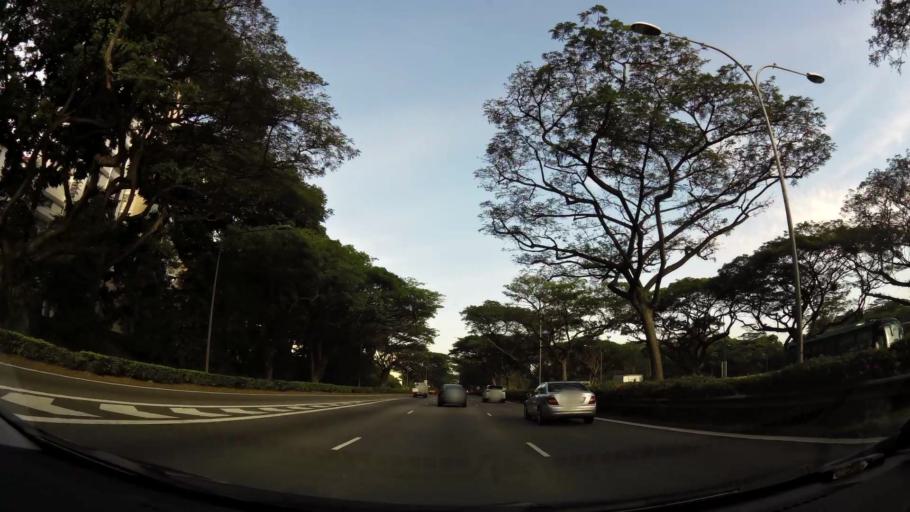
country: MY
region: Johor
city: Johor Bahru
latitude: 1.3483
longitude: 103.7347
